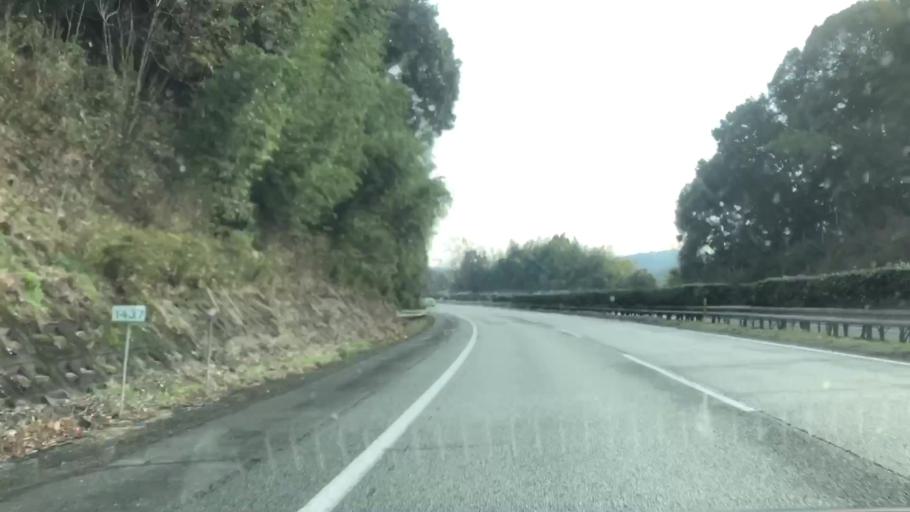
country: JP
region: Kumamoto
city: Tamana
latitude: 33.0060
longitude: 130.5830
